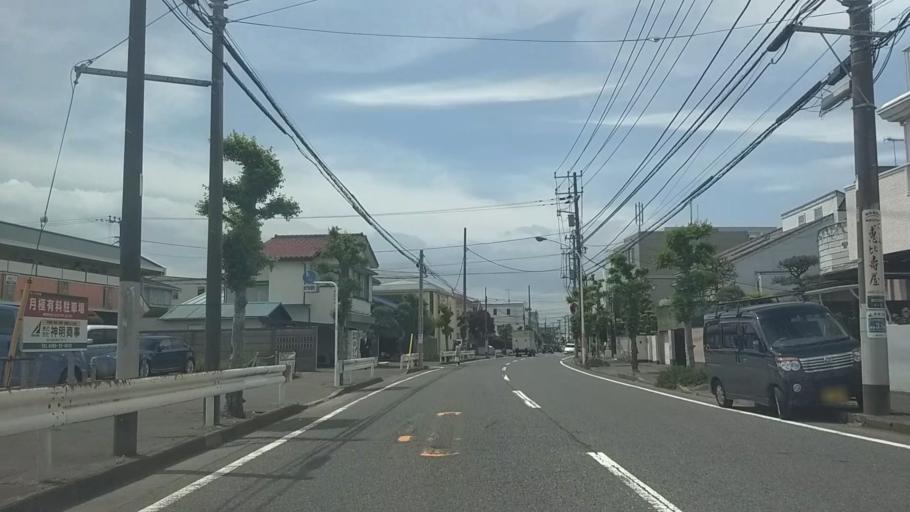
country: JP
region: Kanagawa
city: Fujisawa
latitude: 35.3268
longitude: 139.4676
